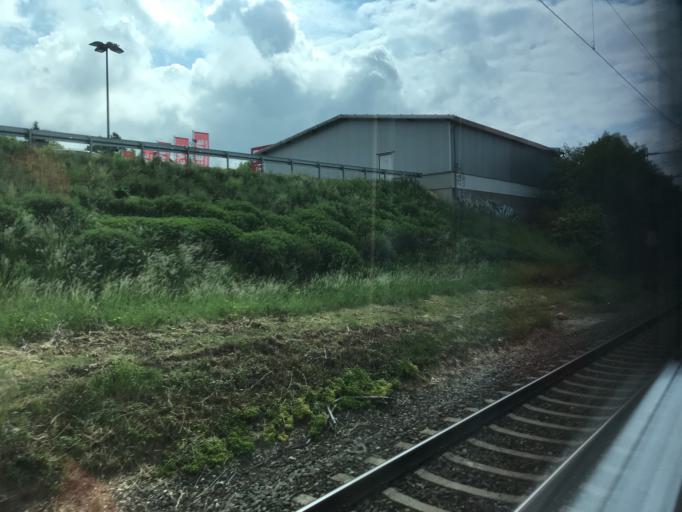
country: DE
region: Baden-Wuerttemberg
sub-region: Tuebingen Region
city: Lonsee
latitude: 48.5362
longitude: 9.9234
